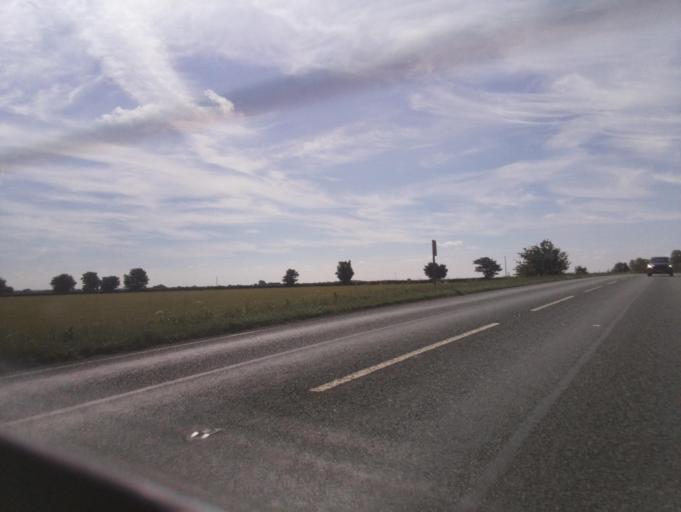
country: GB
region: England
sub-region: Lincolnshire
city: Burton
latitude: 53.3575
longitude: -0.5452
